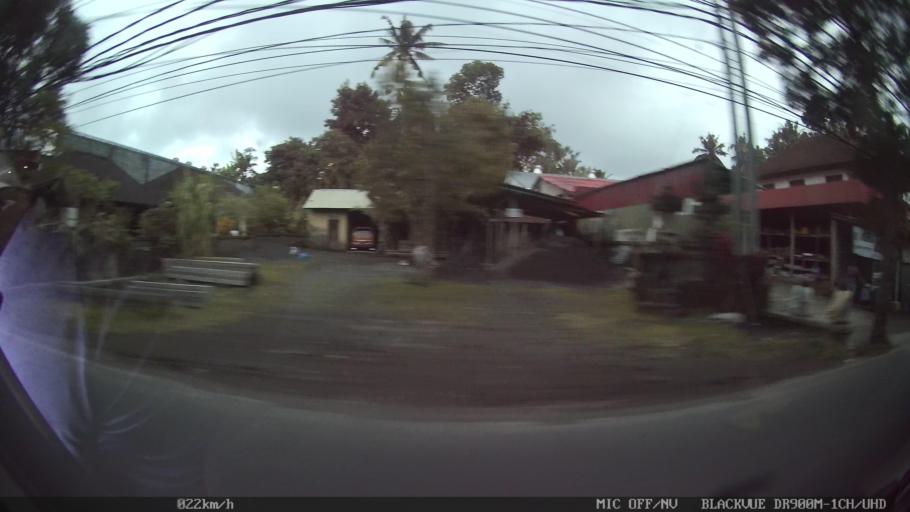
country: ID
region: Bali
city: Bayad
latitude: -8.4448
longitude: 115.2421
